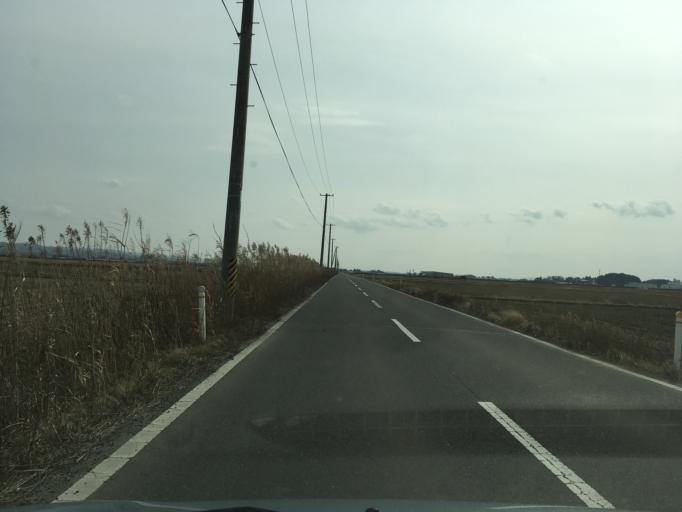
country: JP
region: Iwate
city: Ichinoseki
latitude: 38.7452
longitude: 141.2375
